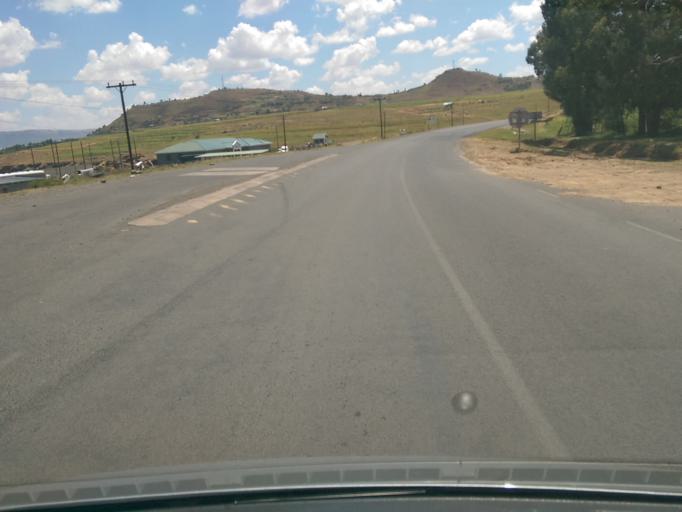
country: LS
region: Maseru
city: Maseru
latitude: -29.4202
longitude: 27.6454
